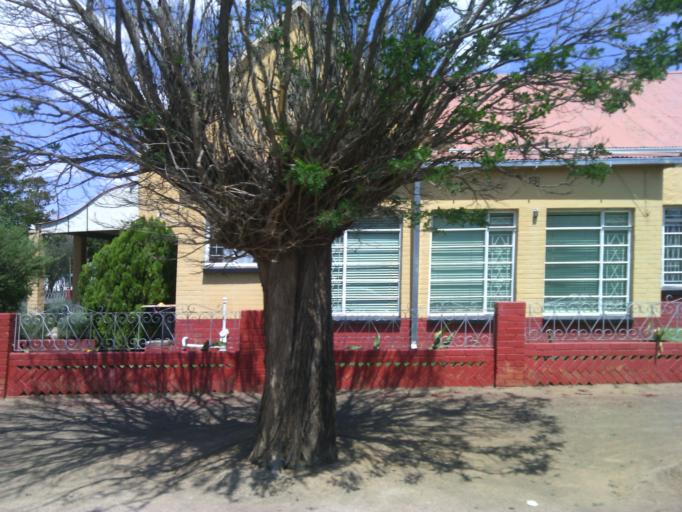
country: ZA
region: Orange Free State
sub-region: Xhariep District Municipality
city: Dewetsdorp
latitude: -29.5850
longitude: 26.6643
